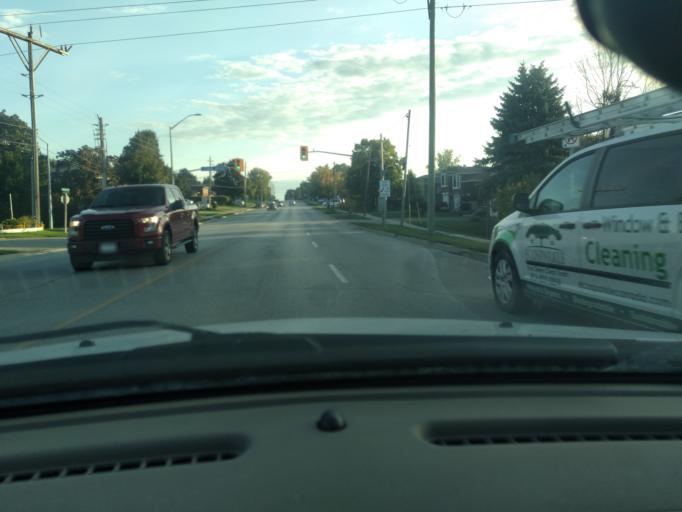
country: CA
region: Ontario
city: Bradford West Gwillimbury
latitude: 44.1035
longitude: -79.5682
